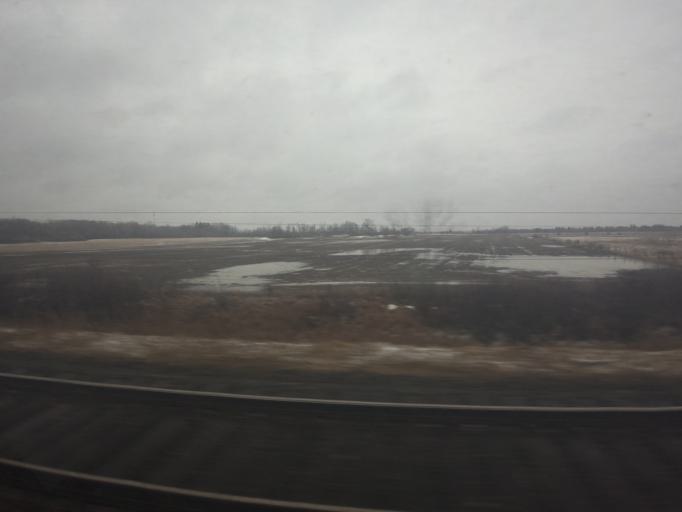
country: CA
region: Ontario
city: Gananoque
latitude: 44.3395
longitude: -76.2891
